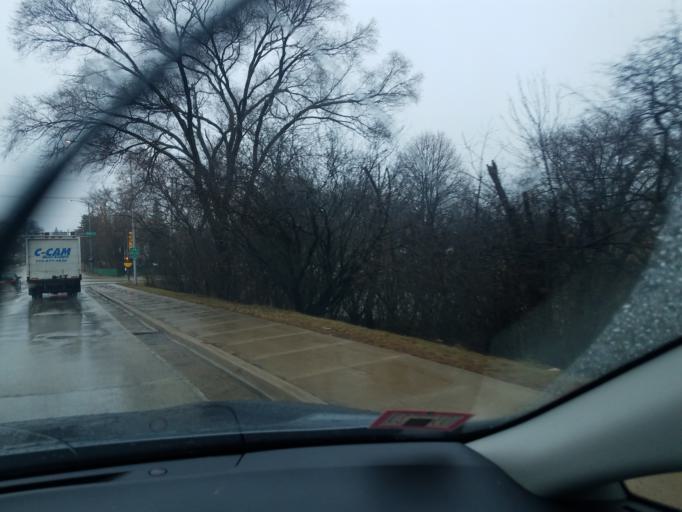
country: US
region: Illinois
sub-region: Cook County
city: Skokie
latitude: 42.0194
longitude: -87.7595
